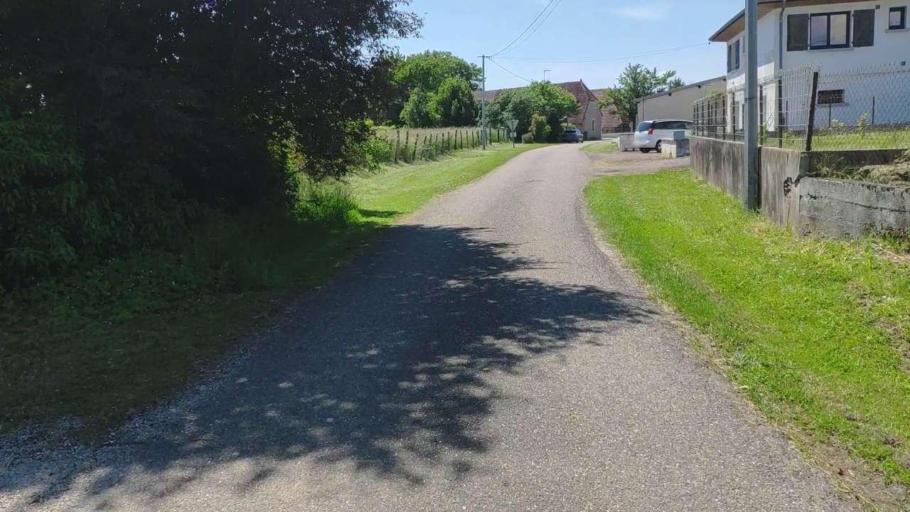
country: FR
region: Franche-Comte
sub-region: Departement du Jura
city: Bletterans
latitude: 46.7424
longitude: 5.3700
